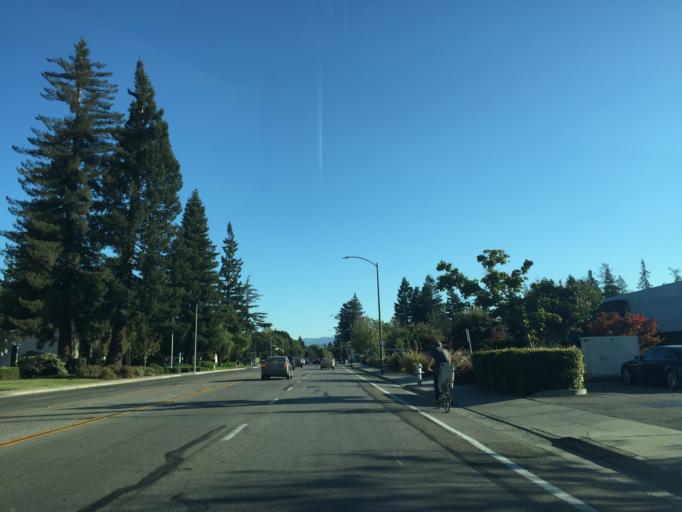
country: US
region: California
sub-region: Santa Clara County
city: Mountain View
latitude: 37.4082
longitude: -122.0782
